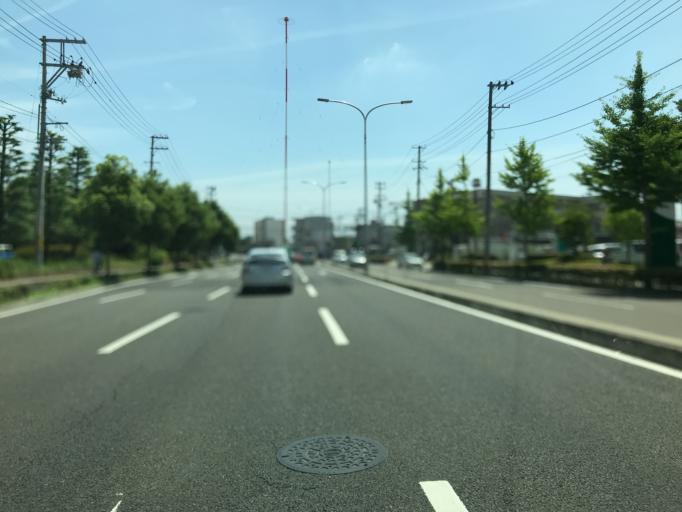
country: JP
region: Miyagi
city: Sendai-shi
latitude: 38.2730
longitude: 140.9060
